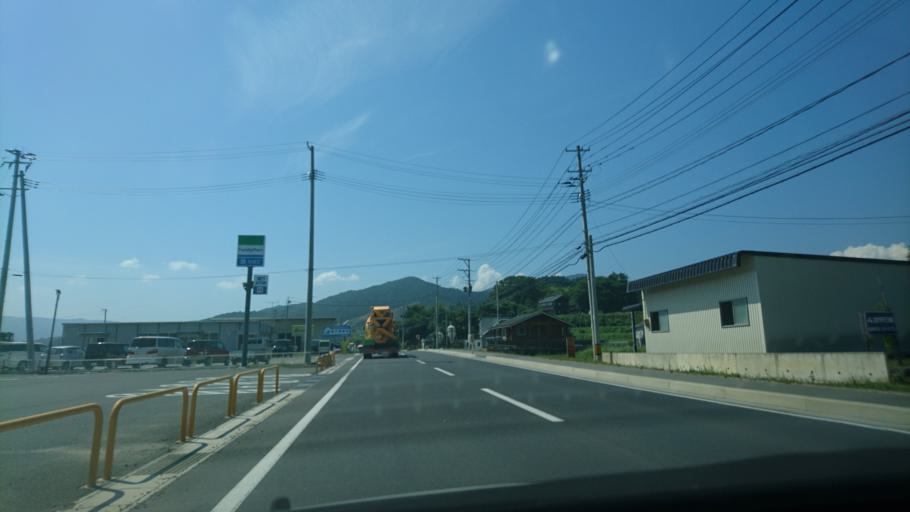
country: JP
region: Iwate
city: Ofunato
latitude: 39.0336
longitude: 141.6124
